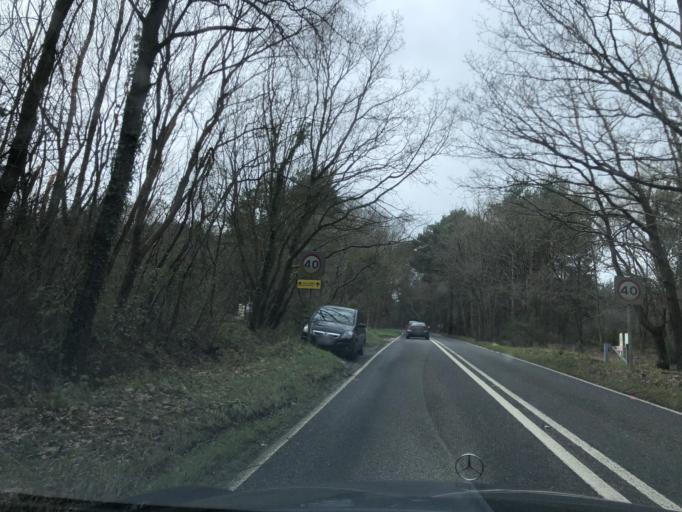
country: GB
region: England
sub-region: Surrey
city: Pirbright
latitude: 51.2975
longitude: -0.6886
